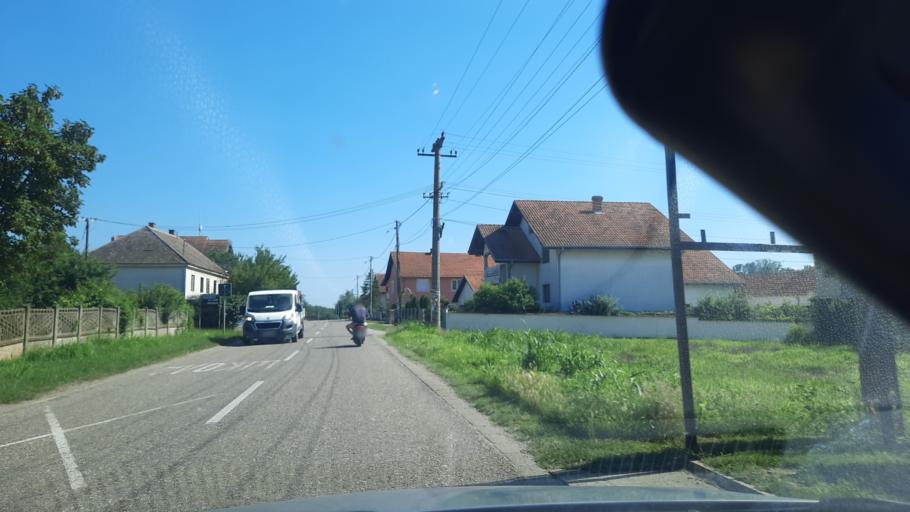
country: RS
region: Central Serbia
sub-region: Branicevski Okrug
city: Malo Crnice
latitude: 44.6119
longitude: 21.2678
